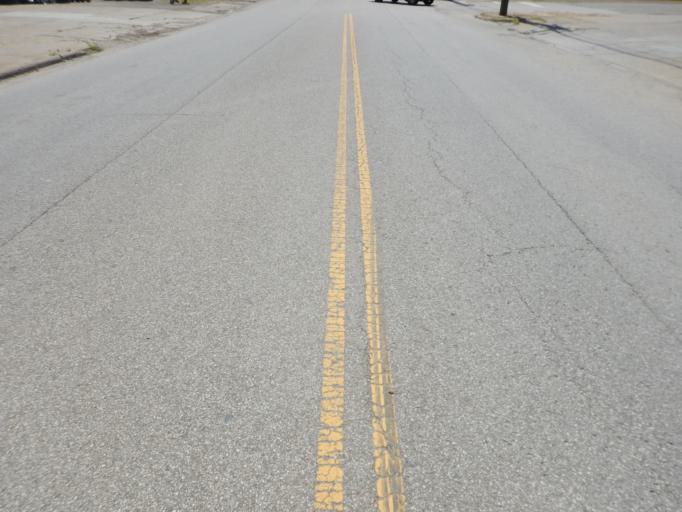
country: US
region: Ohio
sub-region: Muskingum County
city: Zanesville
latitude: 39.9413
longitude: -82.0238
